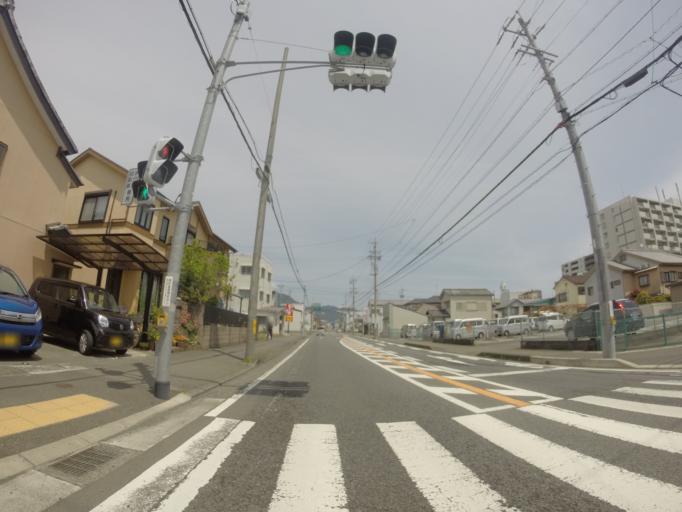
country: JP
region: Shizuoka
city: Yaizu
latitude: 34.8627
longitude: 138.3193
